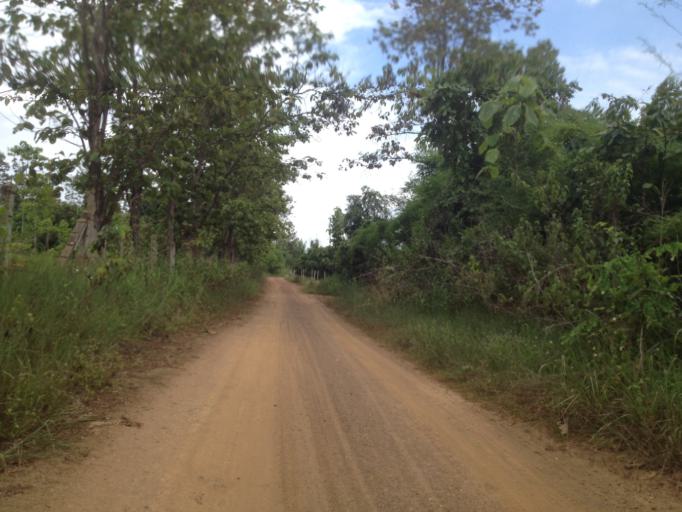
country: TH
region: Chiang Mai
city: Hang Dong
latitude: 18.7118
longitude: 98.8778
